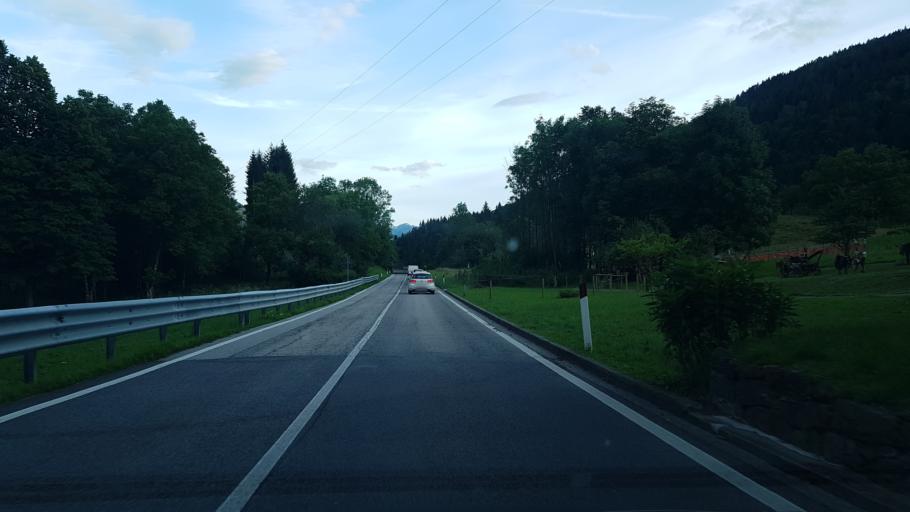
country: IT
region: Friuli Venezia Giulia
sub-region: Provincia di Udine
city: Rigolato
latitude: 46.5399
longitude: 12.8648
